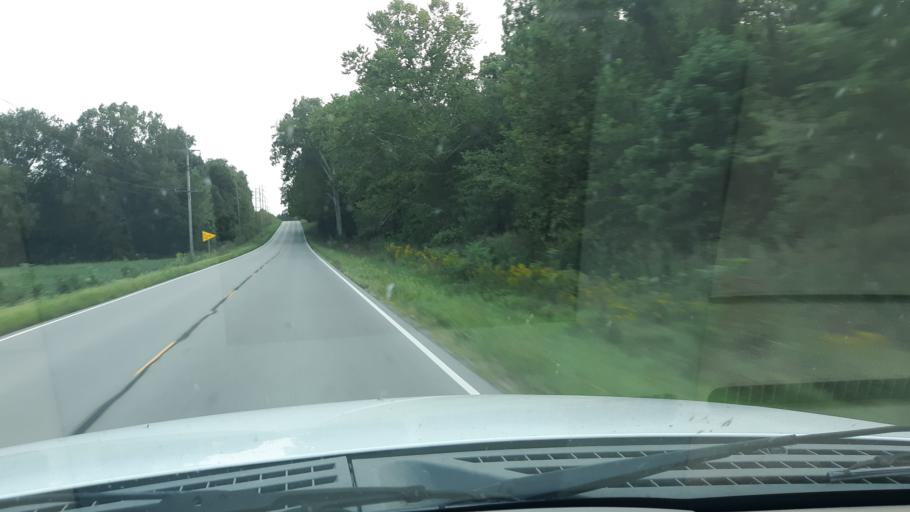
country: US
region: Illinois
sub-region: White County
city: Norris City
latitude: 37.9323
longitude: -88.3468
